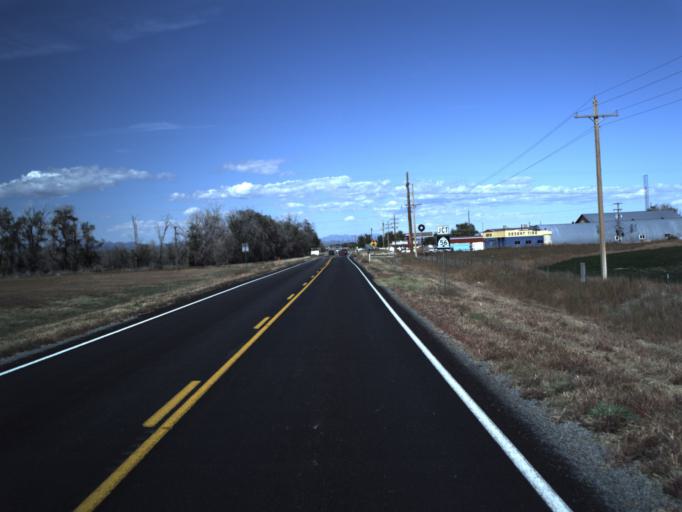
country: US
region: Utah
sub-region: Washington County
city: Enterprise
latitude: 37.7056
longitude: -113.6564
